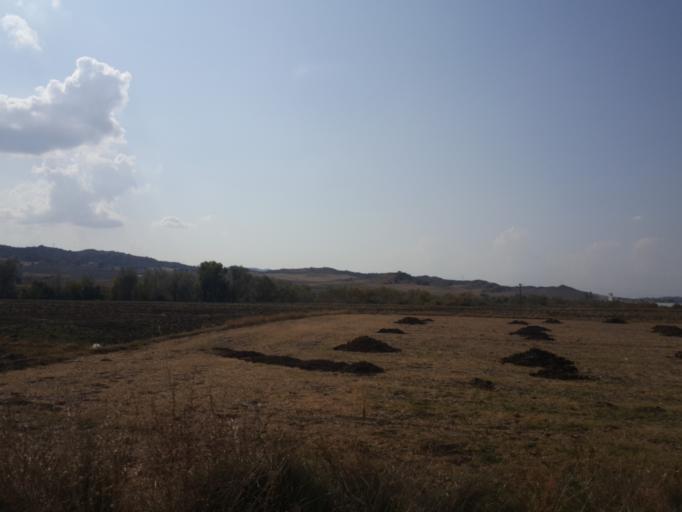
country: TR
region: Corum
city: Sungurlu
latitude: 40.1750
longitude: 34.4671
